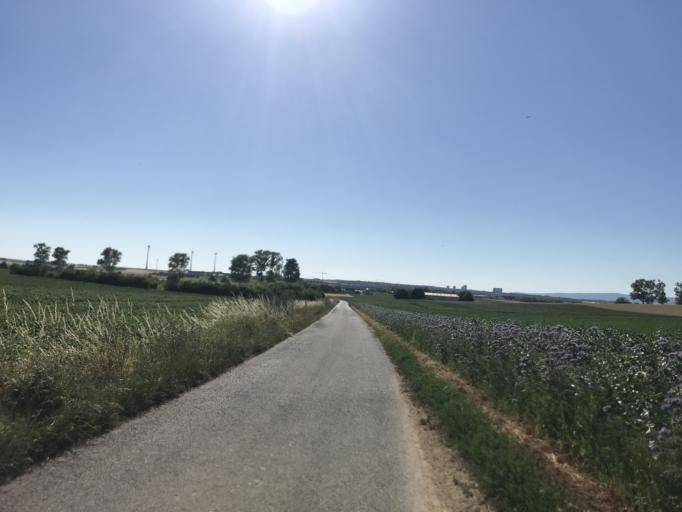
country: DE
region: Rheinland-Pfalz
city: Gau-Bischofsheim
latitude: 49.9426
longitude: 8.2851
